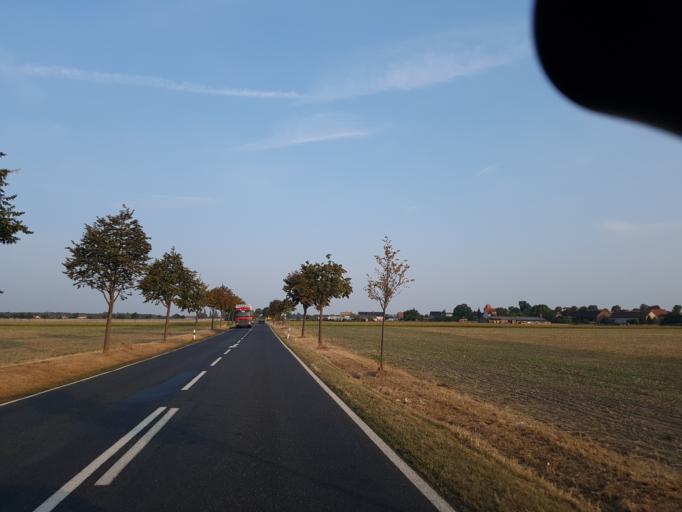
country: DE
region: Saxony
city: Elsnig
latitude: 51.6062
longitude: 12.9321
